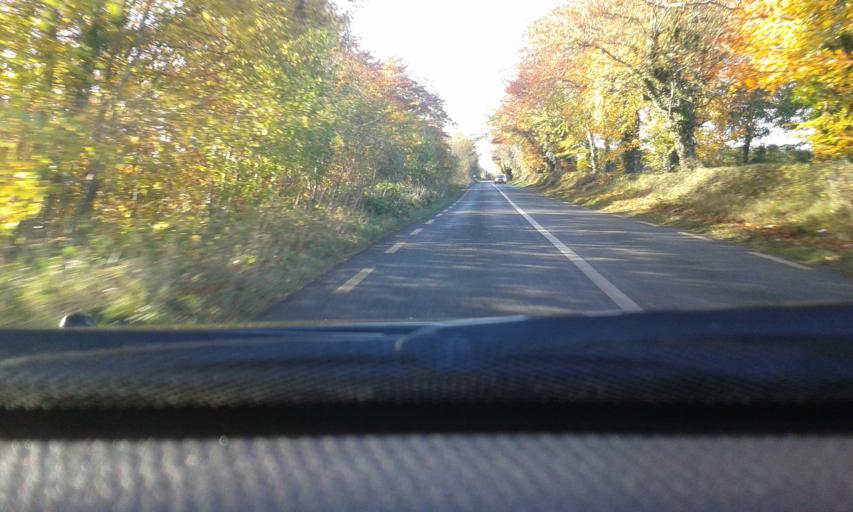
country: IE
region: Leinster
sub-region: Kildare
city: Monasterevin
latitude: 53.1578
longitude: -7.0416
